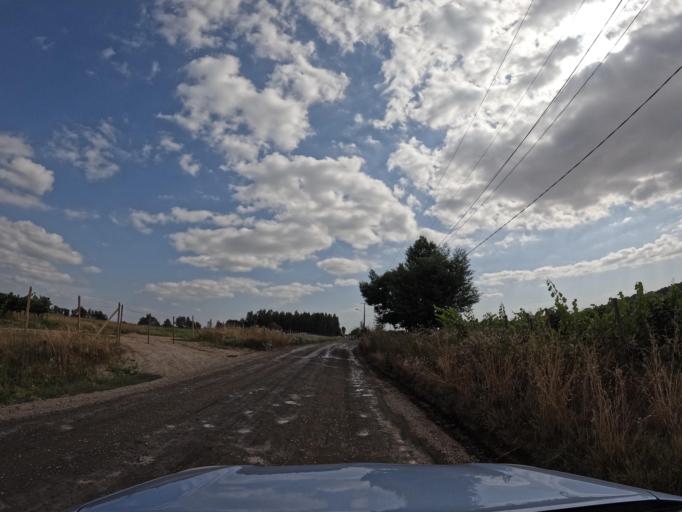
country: CL
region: Maule
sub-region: Provincia de Curico
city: Molina
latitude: -35.1646
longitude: -71.2890
